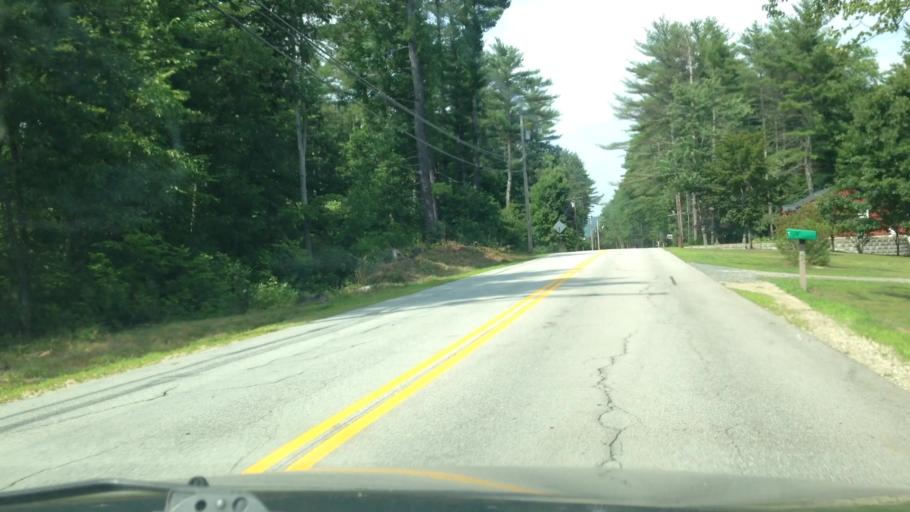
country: US
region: New Hampshire
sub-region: Cheshire County
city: Swanzey
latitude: 42.8531
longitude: -72.2533
